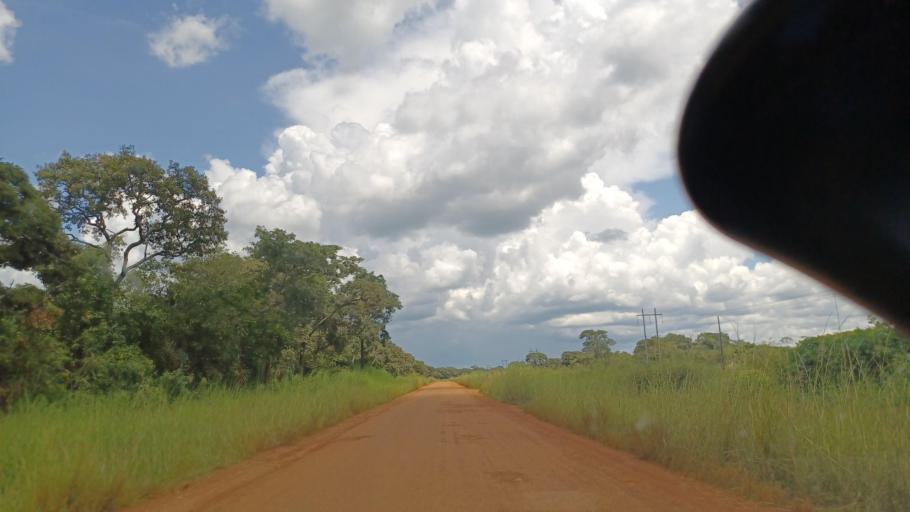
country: ZM
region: North-Western
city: Solwezi
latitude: -12.6891
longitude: 26.0404
